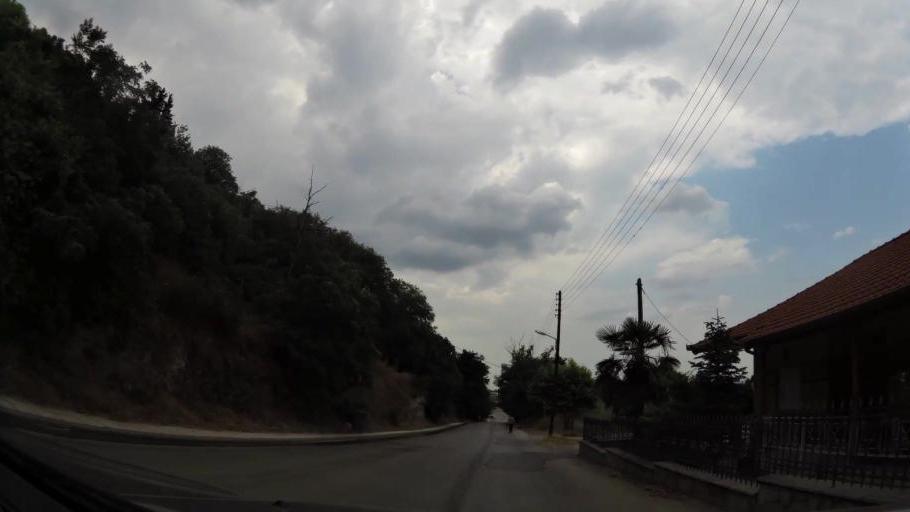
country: GR
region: Central Macedonia
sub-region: Nomos Imathias
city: Veroia
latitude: 40.5260
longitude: 22.2085
